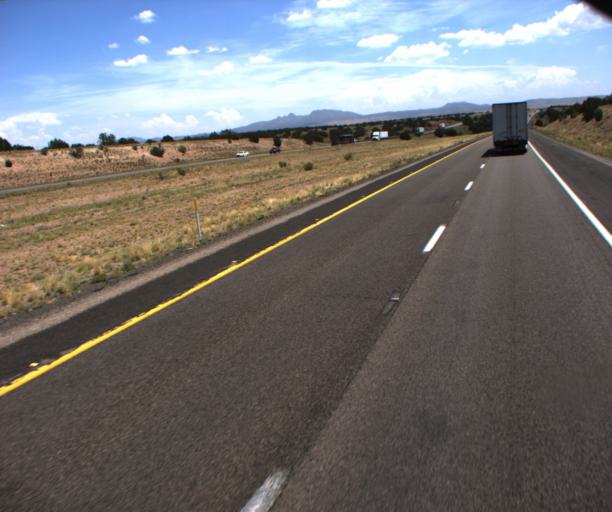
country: US
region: Arizona
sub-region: Mohave County
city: Peach Springs
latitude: 35.3223
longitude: -112.9271
